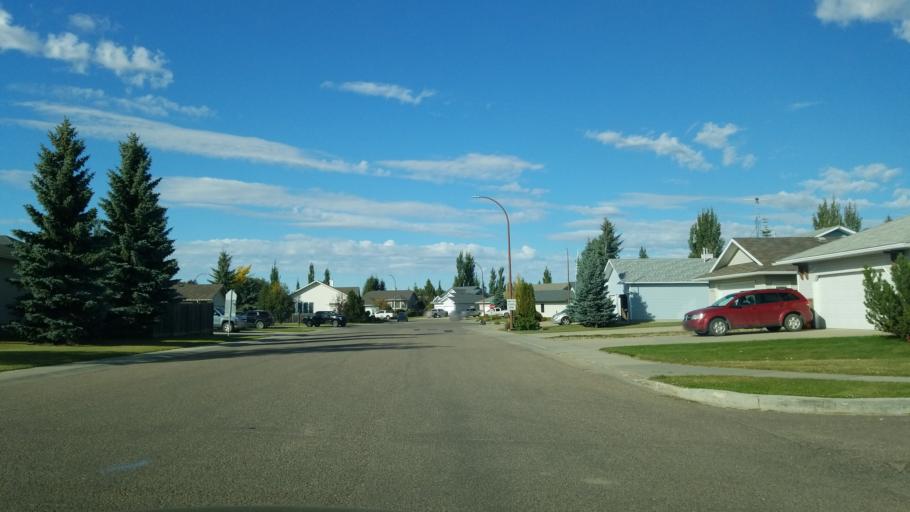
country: CA
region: Saskatchewan
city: Lloydminster
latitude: 53.2567
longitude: -110.0214
